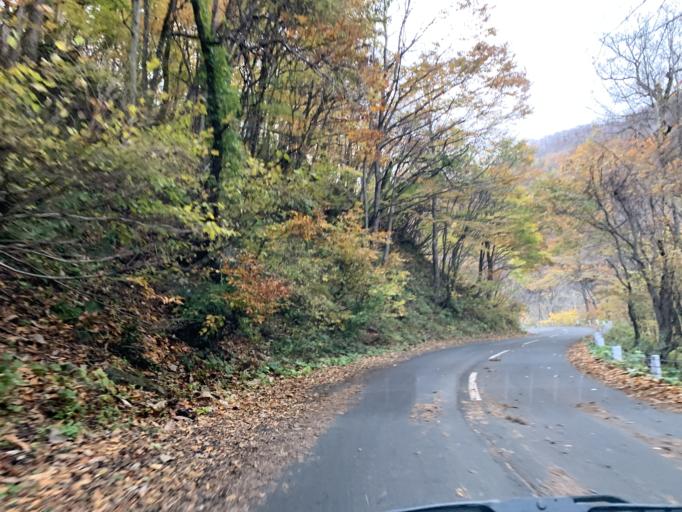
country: JP
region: Iwate
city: Mizusawa
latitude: 39.1166
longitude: 140.8415
